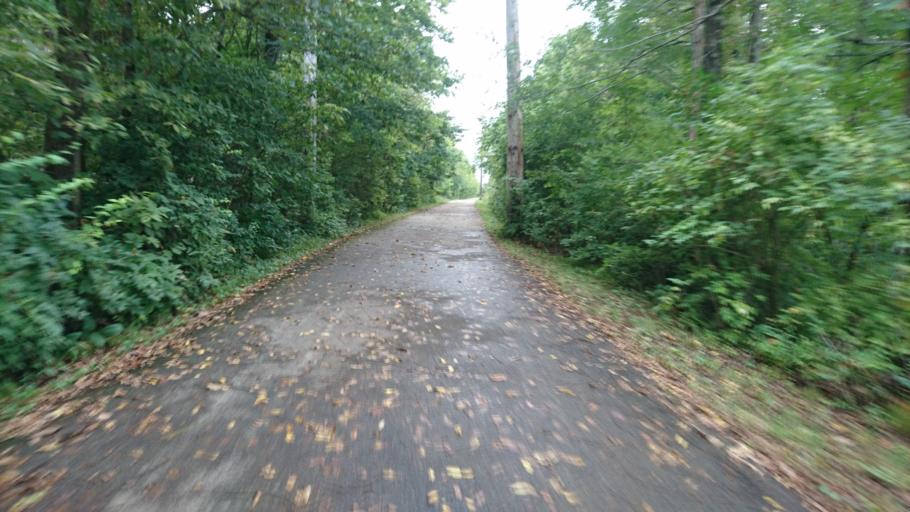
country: US
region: Illinois
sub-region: Sangamon County
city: Chatham
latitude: 39.7027
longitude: -89.6895
